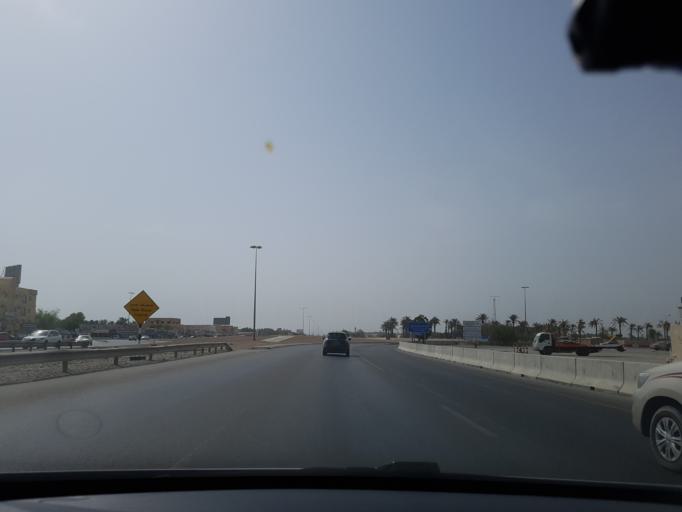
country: OM
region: Al Batinah
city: Al Khaburah
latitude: 23.9722
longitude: 57.0900
